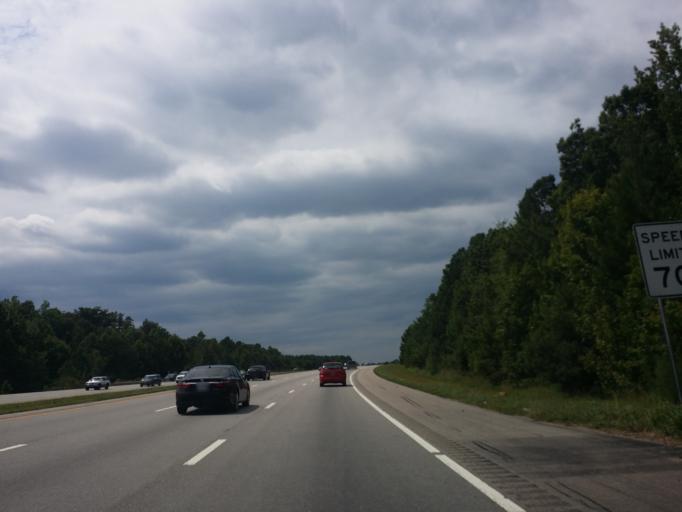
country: US
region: North Carolina
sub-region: Wake County
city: Morrisville
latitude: 35.9092
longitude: -78.7438
